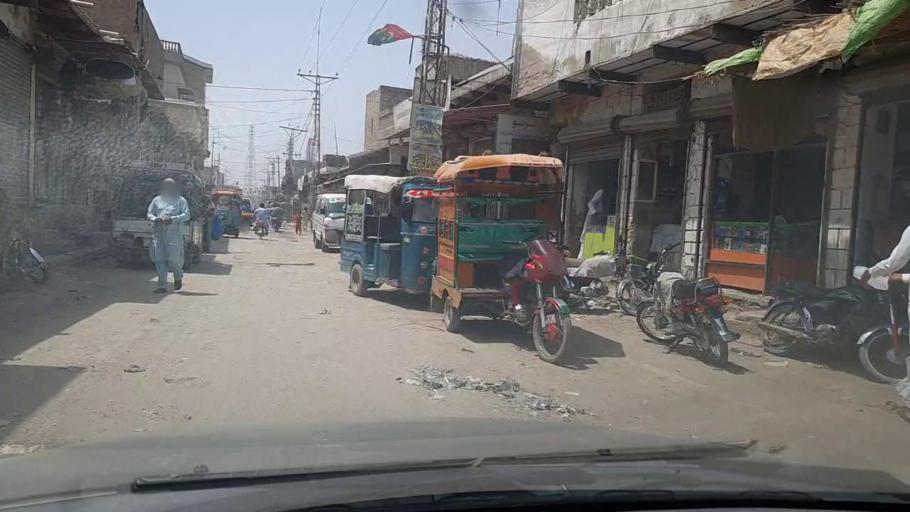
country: PK
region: Sindh
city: Miro Khan
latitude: 27.7612
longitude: 68.0942
